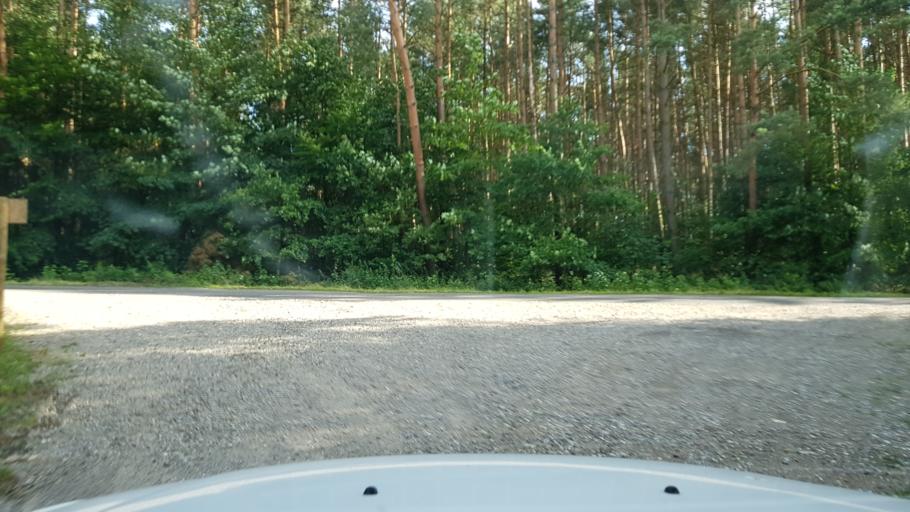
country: PL
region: West Pomeranian Voivodeship
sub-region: Powiat kolobrzeski
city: Grzybowo
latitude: 54.0919
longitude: 15.5340
